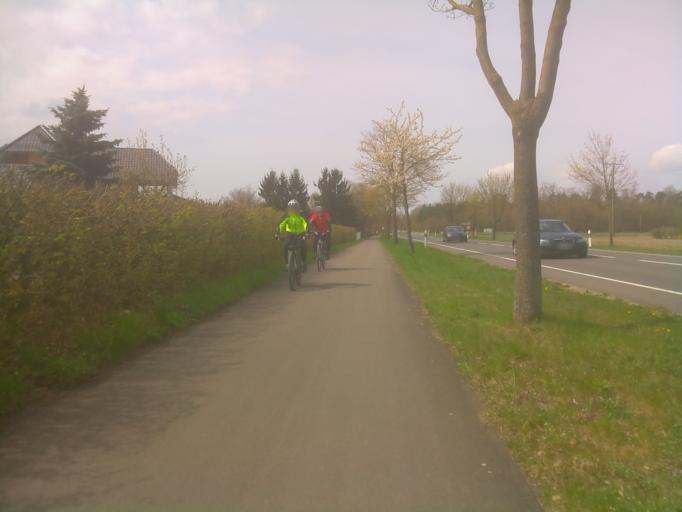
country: DE
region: Hesse
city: Lorsch
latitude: 49.5991
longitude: 8.5700
